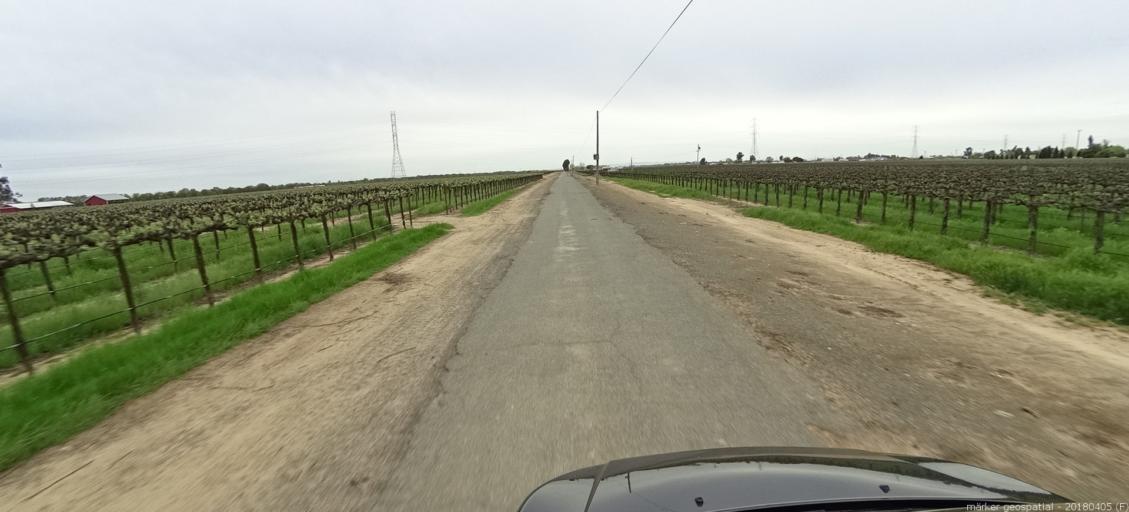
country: US
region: California
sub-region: Sacramento County
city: Herald
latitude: 38.3176
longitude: -121.2307
